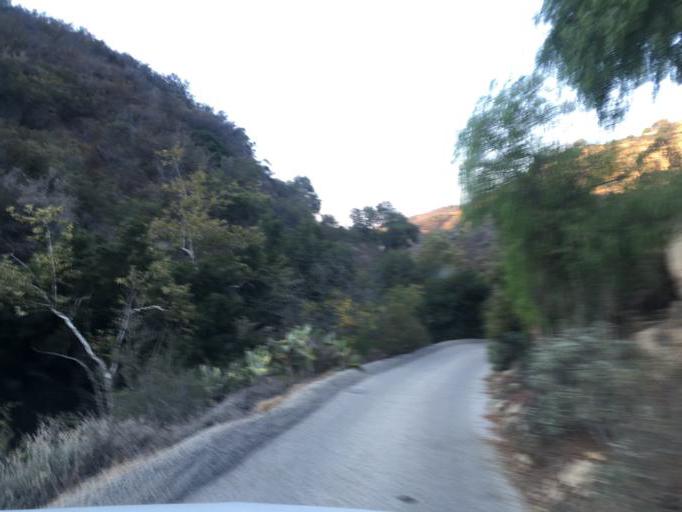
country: US
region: California
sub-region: Los Angeles County
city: Las Flores
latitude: 34.0563
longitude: -118.6373
